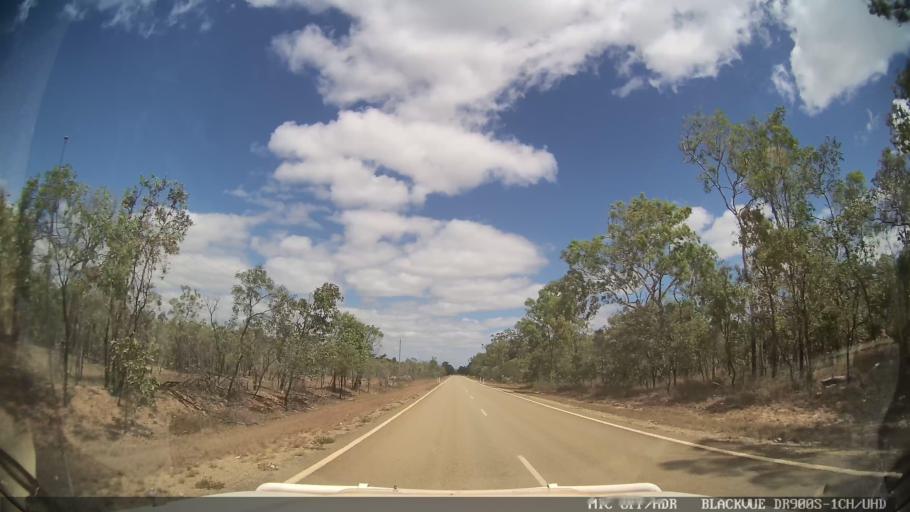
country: AU
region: Queensland
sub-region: Tablelands
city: Ravenshoe
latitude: -17.8128
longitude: 144.9573
